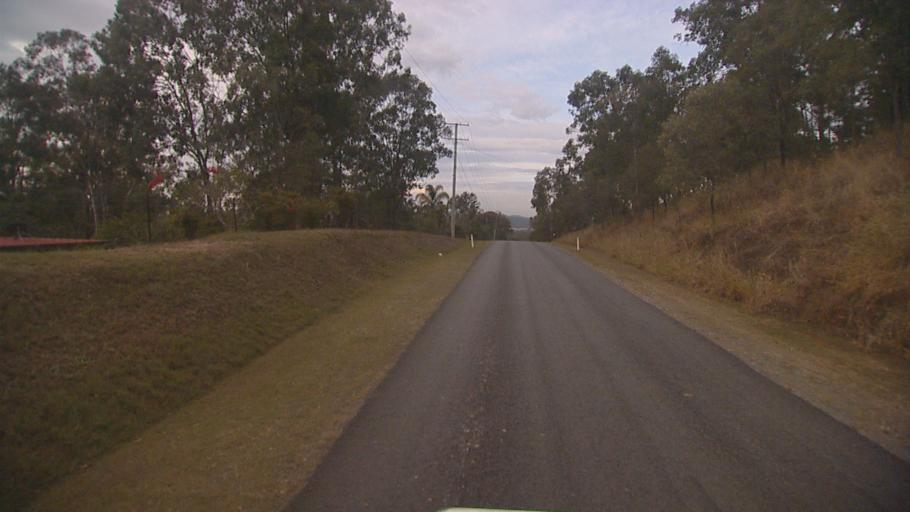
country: AU
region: Queensland
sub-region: Logan
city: Chambers Flat
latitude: -27.8198
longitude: 153.0954
